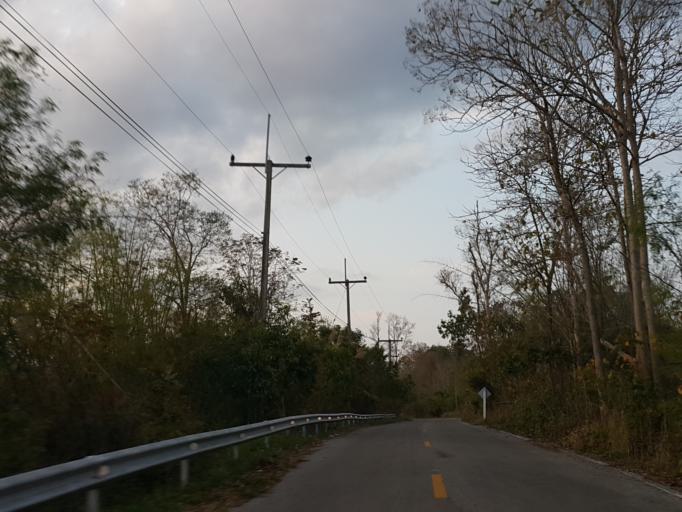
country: TH
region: Lampang
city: Mueang Pan
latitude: 18.8038
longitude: 99.4832
